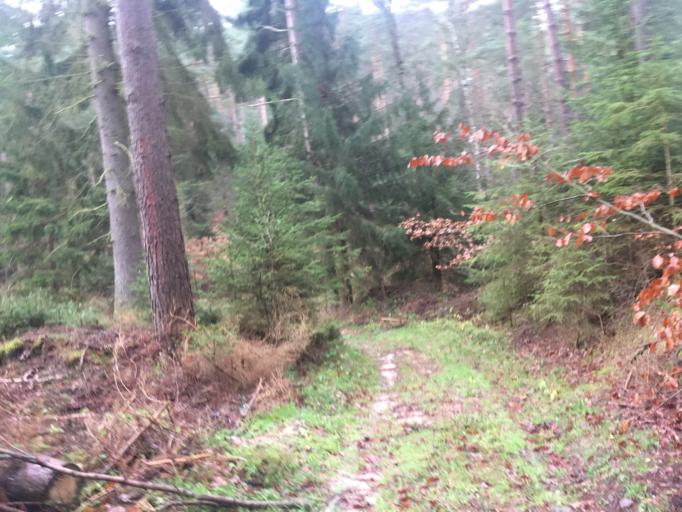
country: DE
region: Thuringia
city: Langenorla
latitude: 50.7195
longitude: 11.5991
